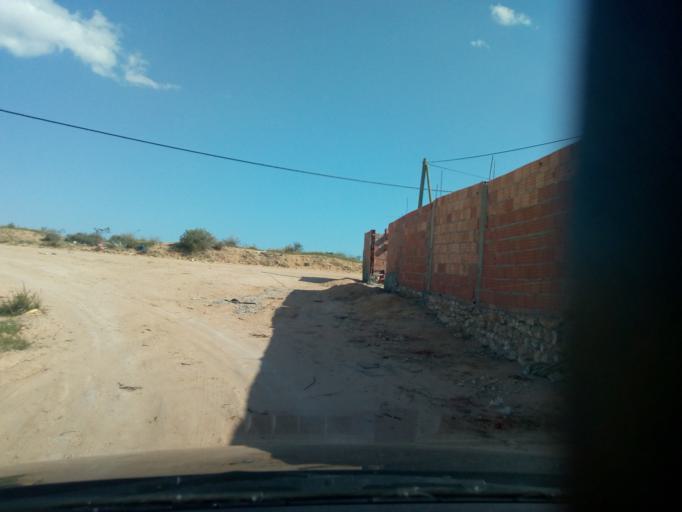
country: TN
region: Safaqis
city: Sfax
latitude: 34.7264
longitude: 10.6046
